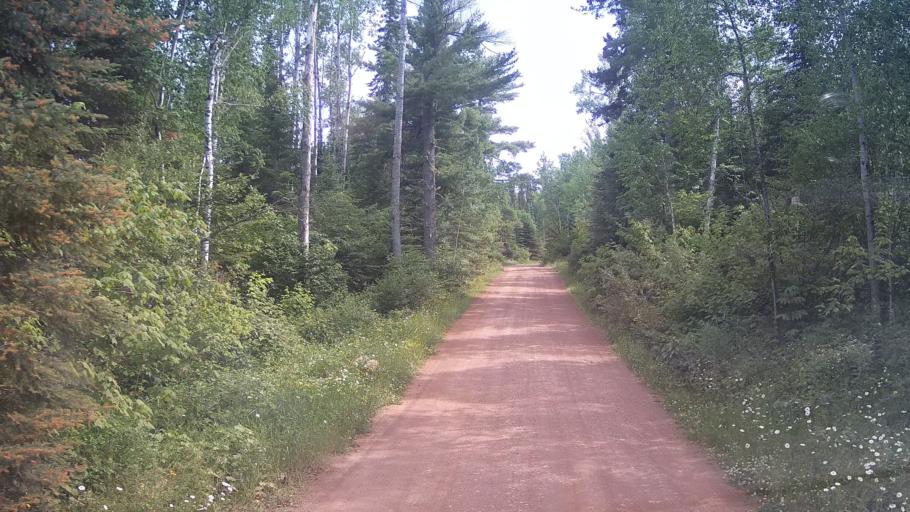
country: CA
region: Ontario
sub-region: Thunder Bay District
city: Thunder Bay
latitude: 48.6821
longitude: -88.6643
